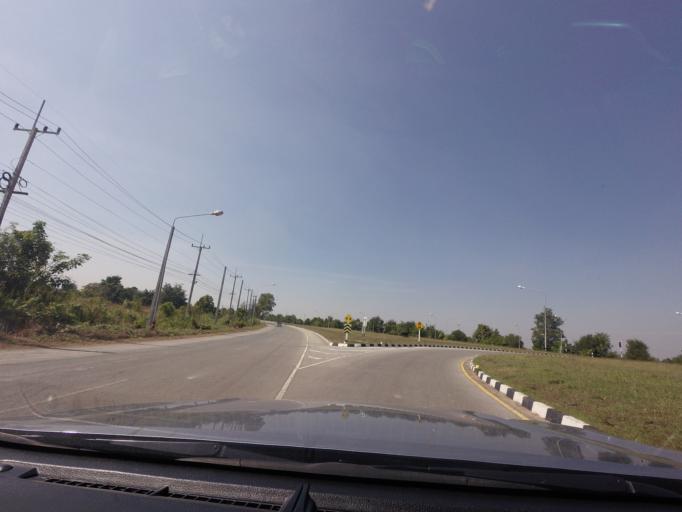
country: TH
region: Sukhothai
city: Ban Na
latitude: 17.0570
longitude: 99.7161
